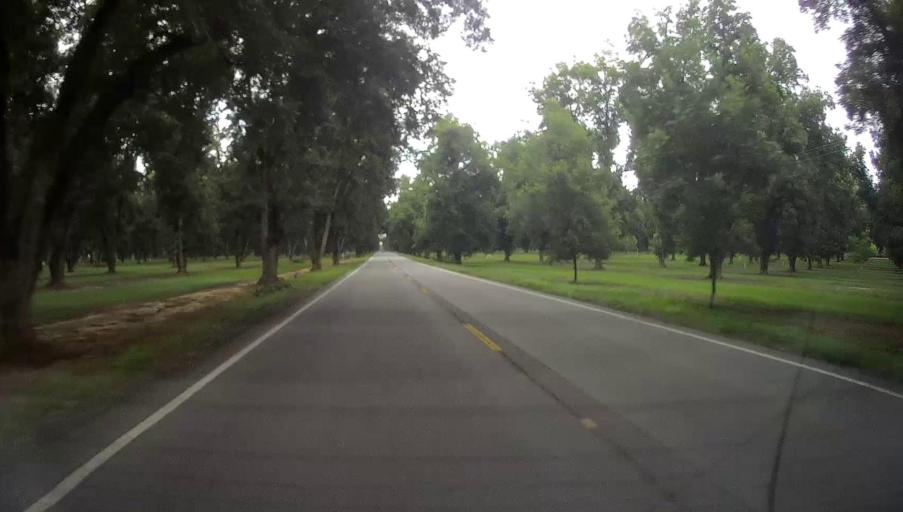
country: US
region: Georgia
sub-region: Houston County
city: Perry
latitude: 32.4417
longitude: -83.6586
